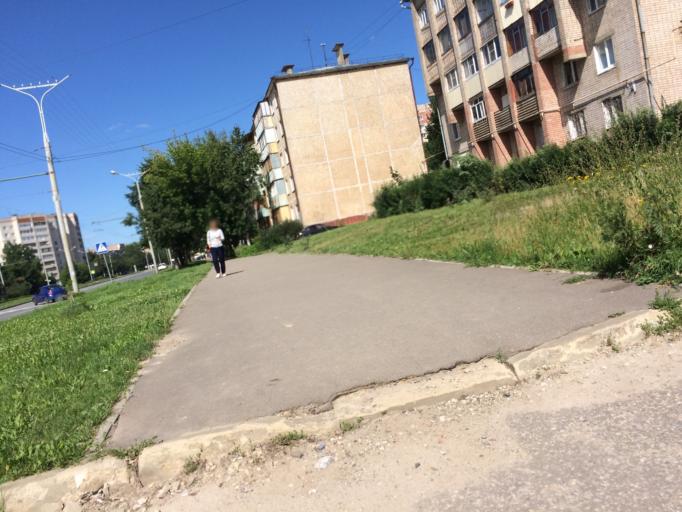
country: RU
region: Mariy-El
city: Yoshkar-Ola
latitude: 56.6301
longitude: 47.9385
